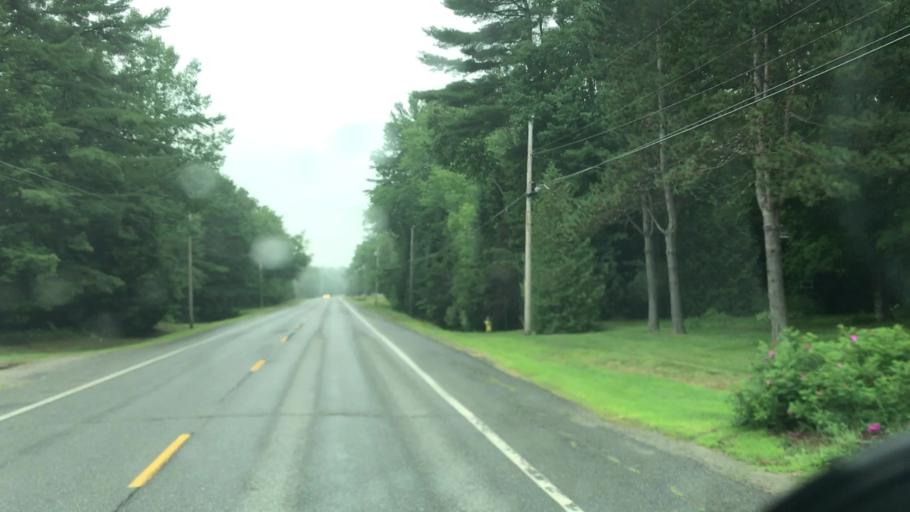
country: US
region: Maine
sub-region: Penobscot County
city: Howland
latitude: 45.2609
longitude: -68.6382
